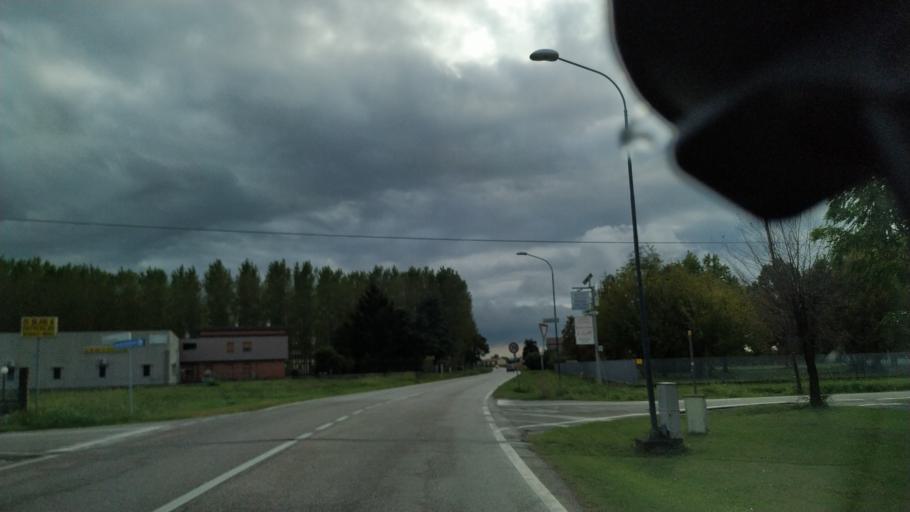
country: IT
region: Emilia-Romagna
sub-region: Provincia di Ferrara
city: Sant'Agostino
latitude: 44.7839
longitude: 11.3632
